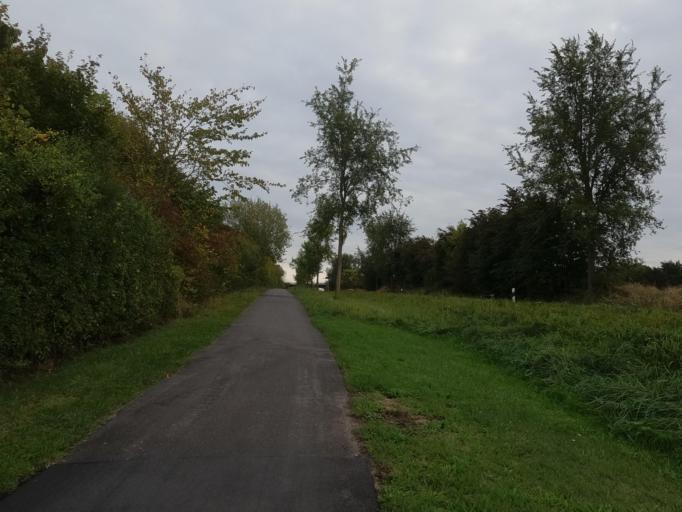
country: DE
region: Schleswig-Holstein
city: Heiligenhafen
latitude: 54.3654
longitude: 11.0274
